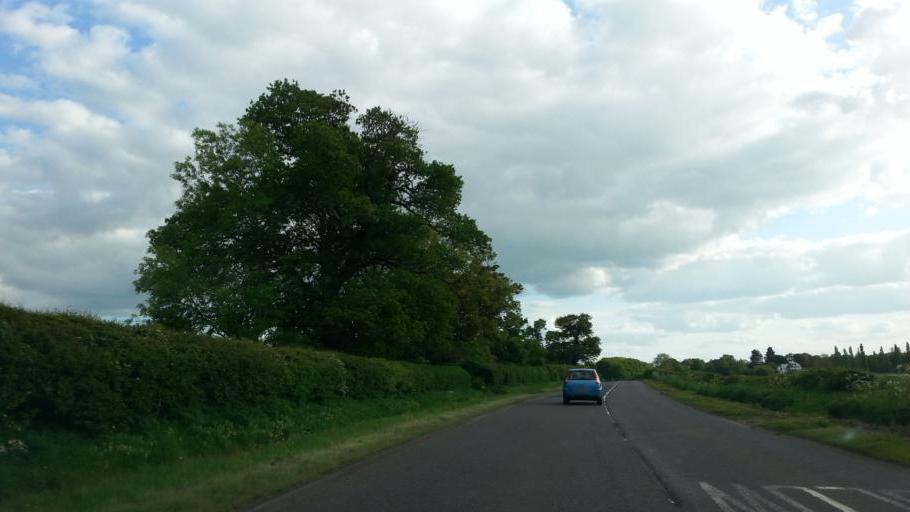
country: GB
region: England
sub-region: Nottinghamshire
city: South Collingham
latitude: 53.1107
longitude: -0.7758
